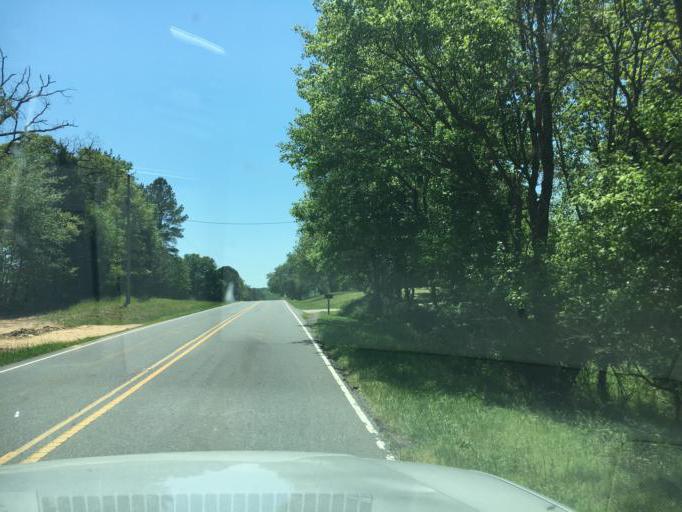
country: US
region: South Carolina
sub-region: Cherokee County
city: Blacksburg
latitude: 35.1919
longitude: -81.5670
